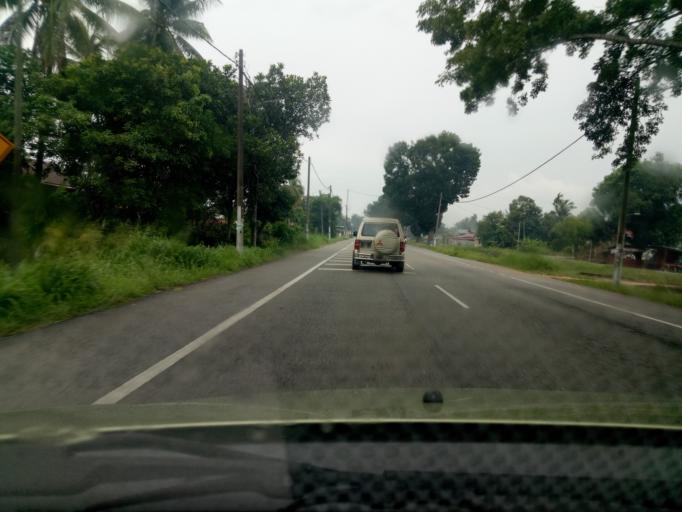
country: MY
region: Kedah
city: Gurun
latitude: 5.9009
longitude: 100.4353
